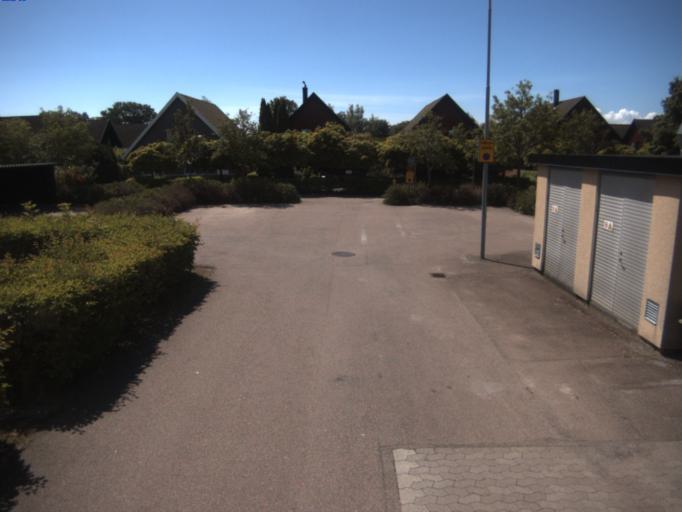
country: SE
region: Skane
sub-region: Helsingborg
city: Rydeback
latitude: 55.9644
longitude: 12.7746
